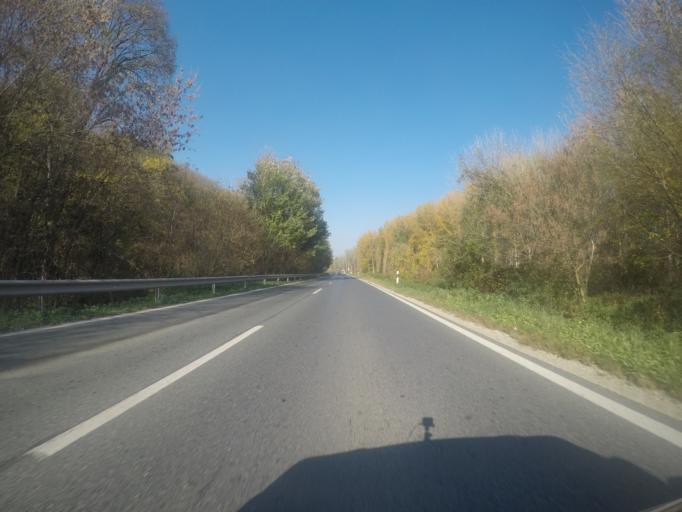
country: HU
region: Tolna
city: Paks
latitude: 46.6505
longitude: 18.8825
